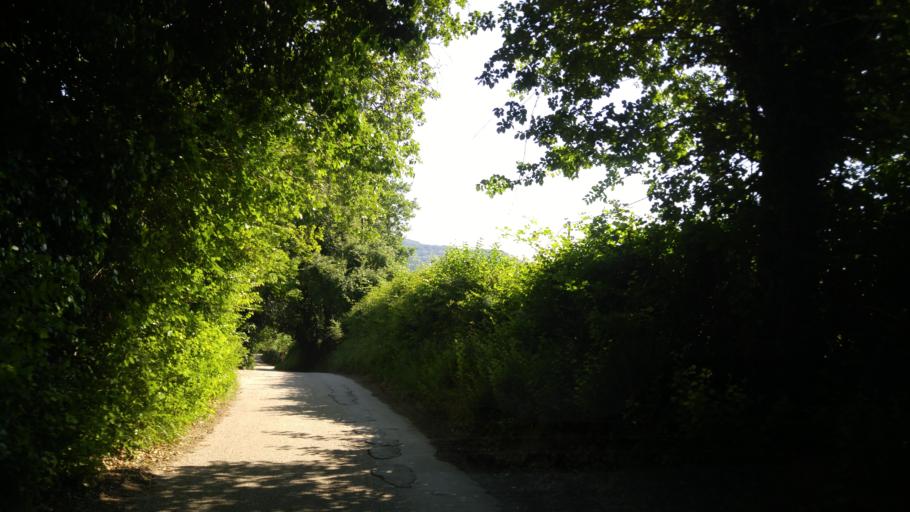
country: IT
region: The Marches
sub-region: Provincia di Pesaro e Urbino
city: Centinarola
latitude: 43.8433
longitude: 12.9875
